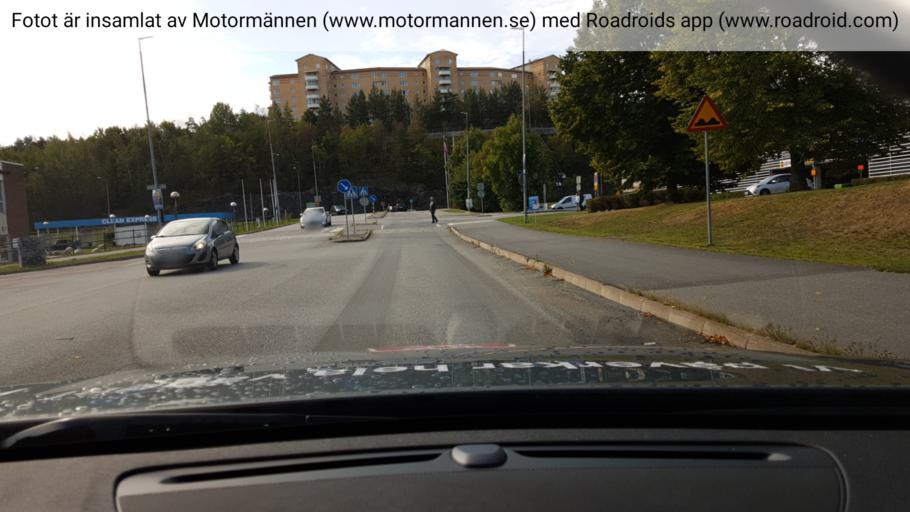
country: SE
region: Stockholm
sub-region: Botkyrka Kommun
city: Eriksberg
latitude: 59.2451
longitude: 17.8292
